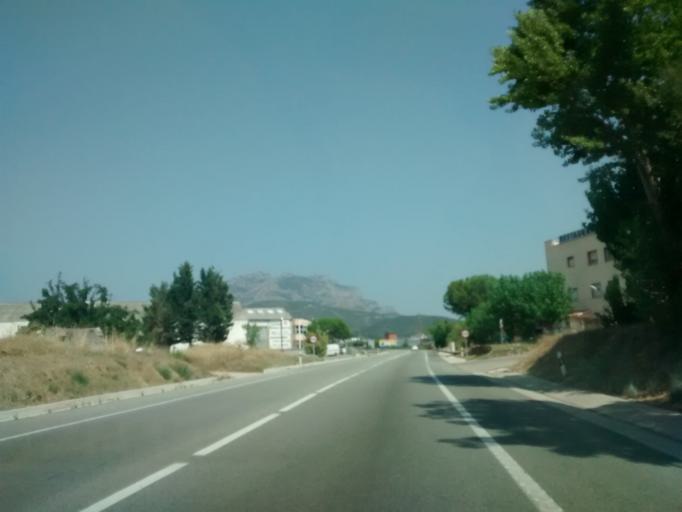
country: ES
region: Catalonia
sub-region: Provincia de Barcelona
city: Olesa de Montserrat
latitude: 41.5403
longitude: 1.8880
